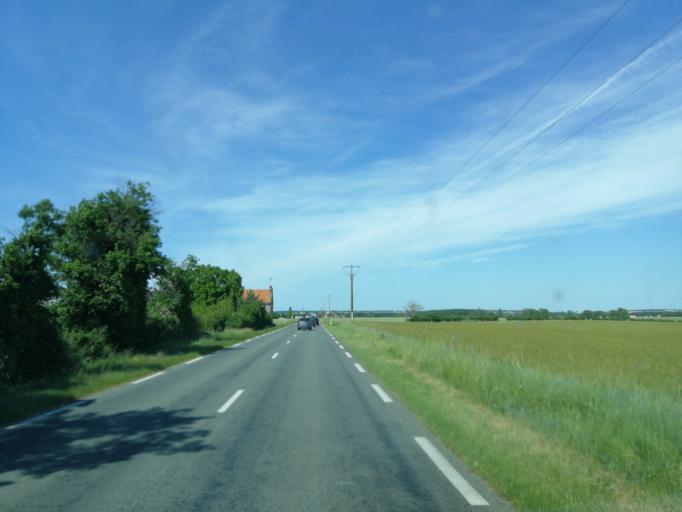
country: FR
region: Poitou-Charentes
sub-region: Departement de la Vienne
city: Loudun
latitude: 47.0707
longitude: 0.1691
